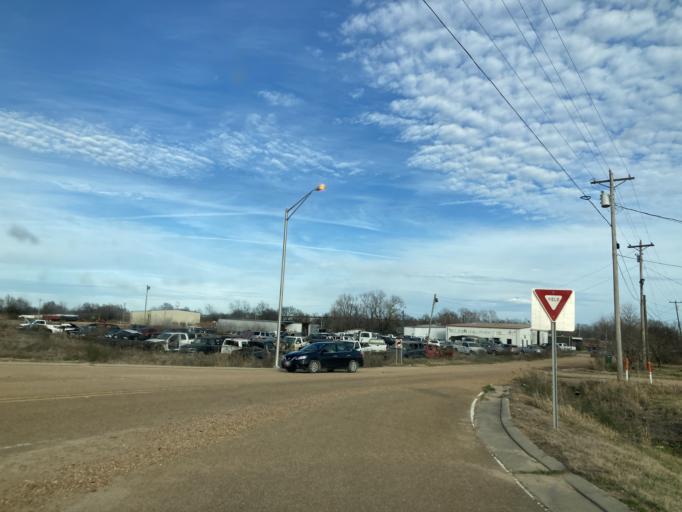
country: US
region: Mississippi
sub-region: Humphreys County
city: Belzoni
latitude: 33.1676
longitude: -90.4984
